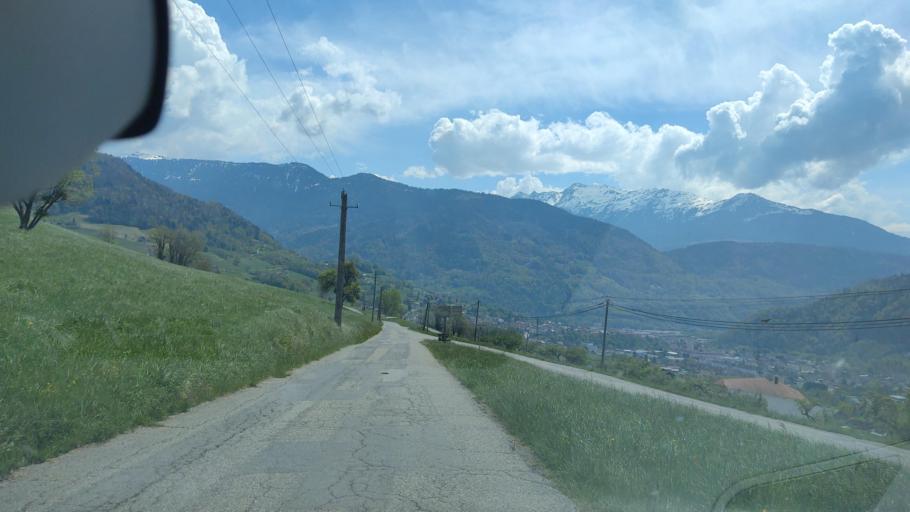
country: FR
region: Rhone-Alpes
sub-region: Departement de la Savoie
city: Ugine
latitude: 45.7671
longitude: 6.4034
